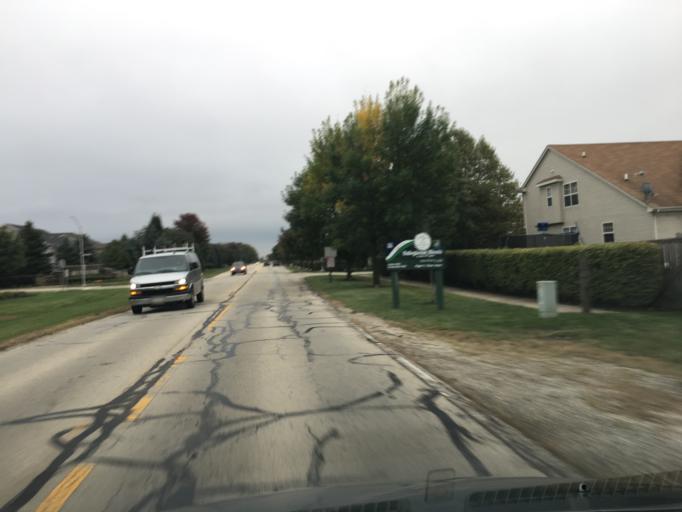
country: US
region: Illinois
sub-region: Will County
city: Plainfield
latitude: 41.6521
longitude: -88.1749
